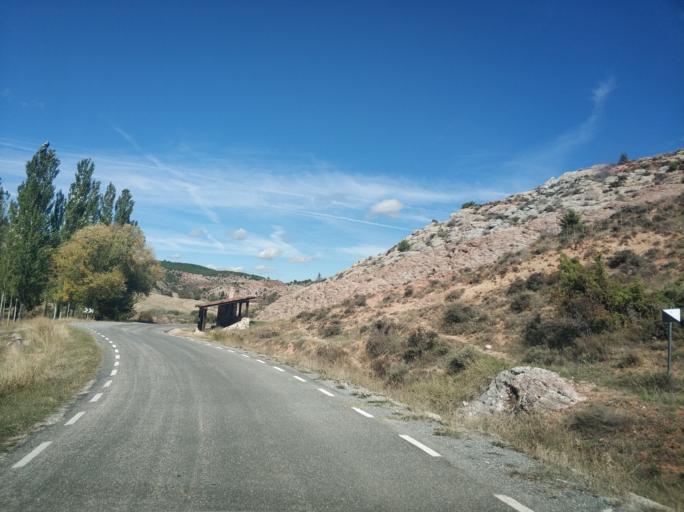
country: ES
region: Castille and Leon
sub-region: Provincia de Soria
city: Espeja de San Marcelino
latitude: 41.8062
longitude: -3.2235
